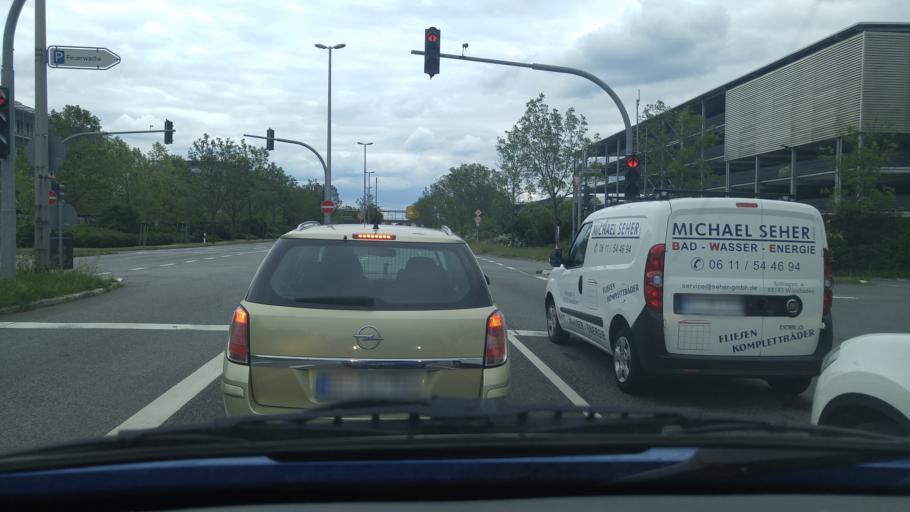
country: DE
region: Hesse
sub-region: Regierungsbezirk Darmstadt
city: Russelsheim
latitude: 49.9851
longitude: 8.4032
